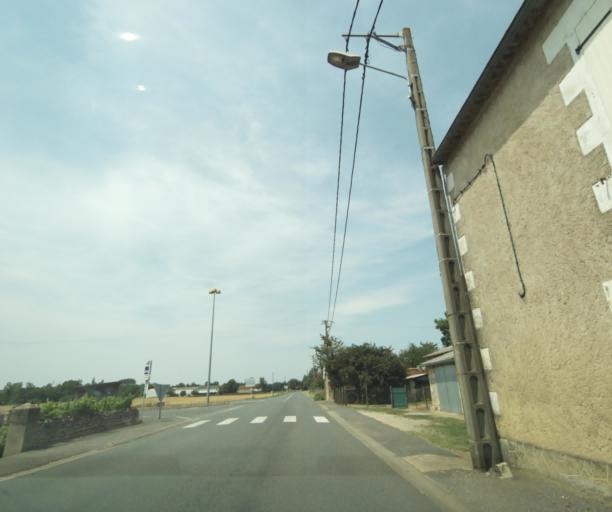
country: FR
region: Poitou-Charentes
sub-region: Departement de la Vienne
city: Chauvigny
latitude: 46.4841
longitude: 0.6546
